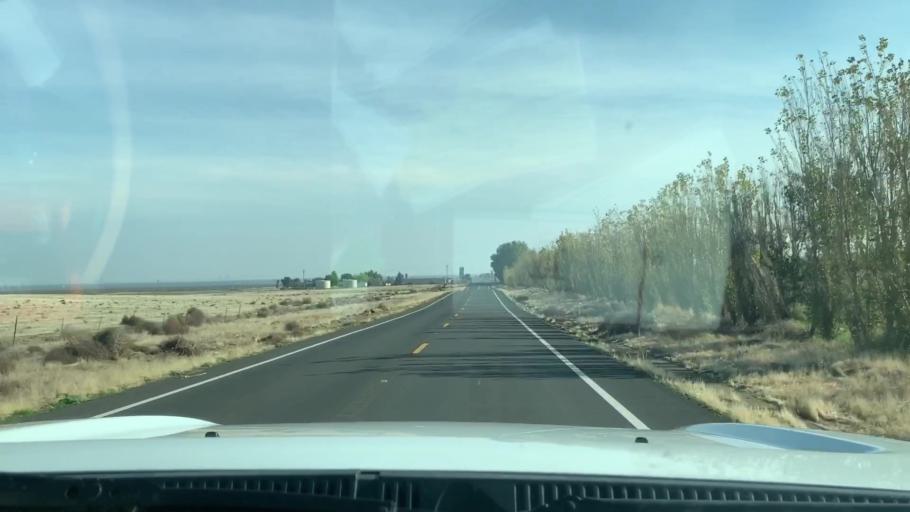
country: US
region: California
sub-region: Fresno County
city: Coalinga
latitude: 36.2541
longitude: -120.2608
